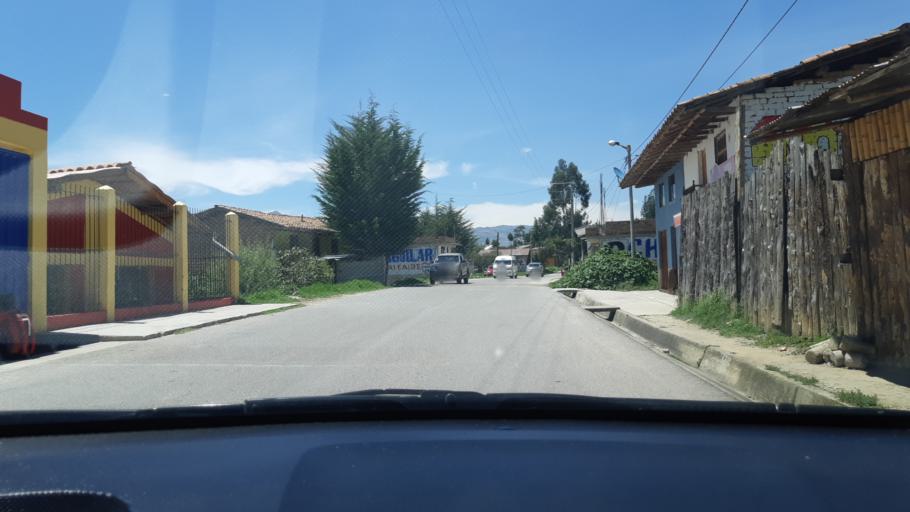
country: PE
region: Cajamarca
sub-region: Provincia de Cajamarca
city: Llacanora
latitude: -7.1830
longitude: -78.4484
